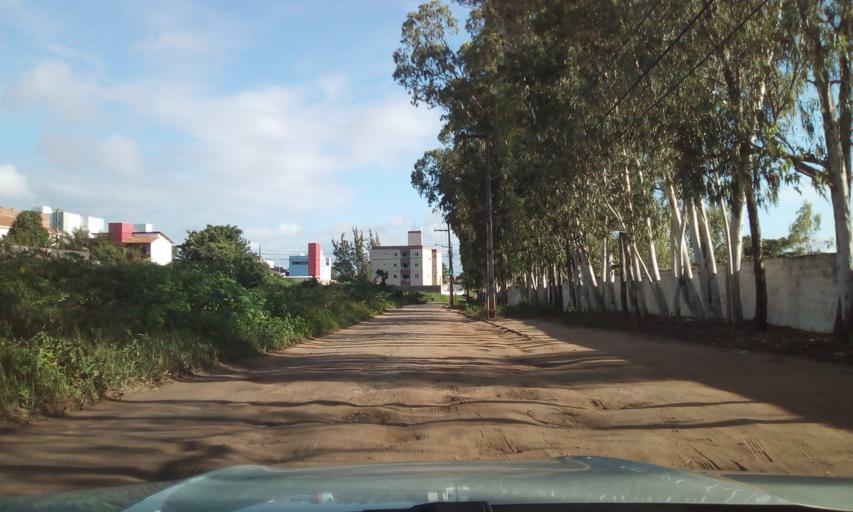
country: BR
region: Paraiba
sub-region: Joao Pessoa
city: Joao Pessoa
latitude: -7.1571
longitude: -34.8493
